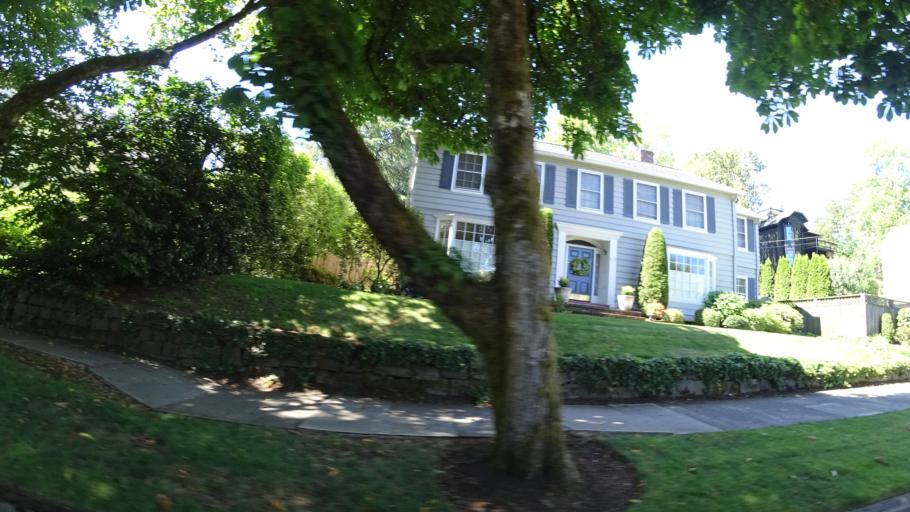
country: US
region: Oregon
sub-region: Multnomah County
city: Portland
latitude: 45.5087
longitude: -122.6970
